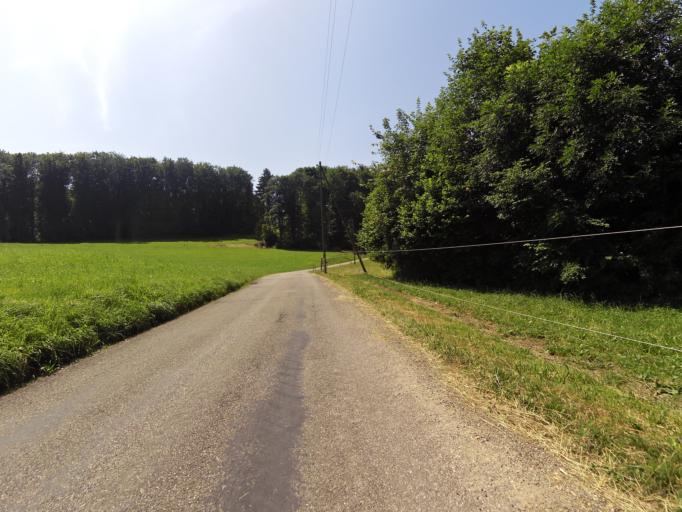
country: CH
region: Thurgau
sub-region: Frauenfeld District
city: Mullheim
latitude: 47.5646
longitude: 8.9974
